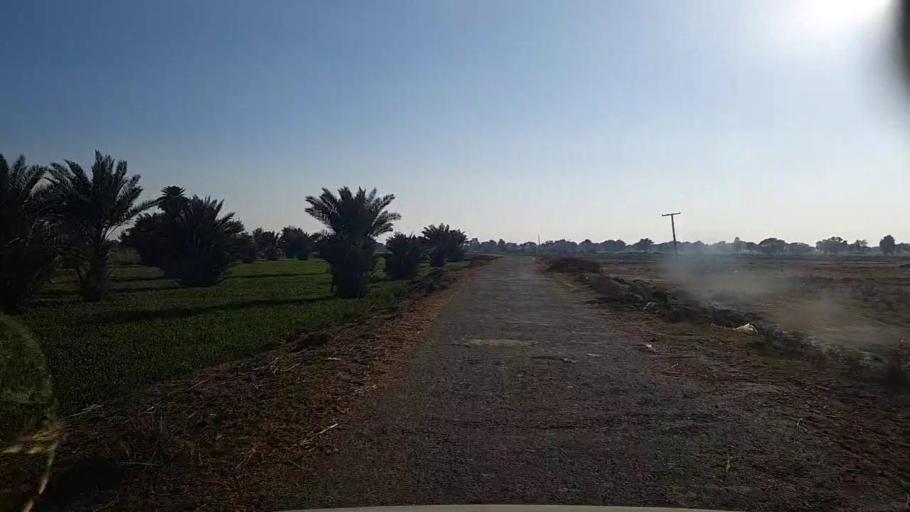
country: PK
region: Sindh
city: Khairpur
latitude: 28.0087
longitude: 69.7210
